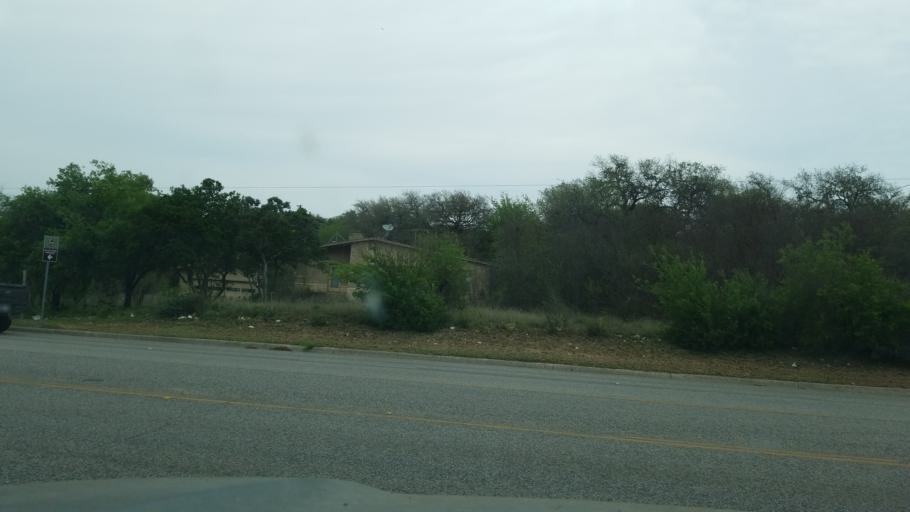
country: US
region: Texas
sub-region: Bexar County
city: Hollywood Park
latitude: 29.5677
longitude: -98.4862
